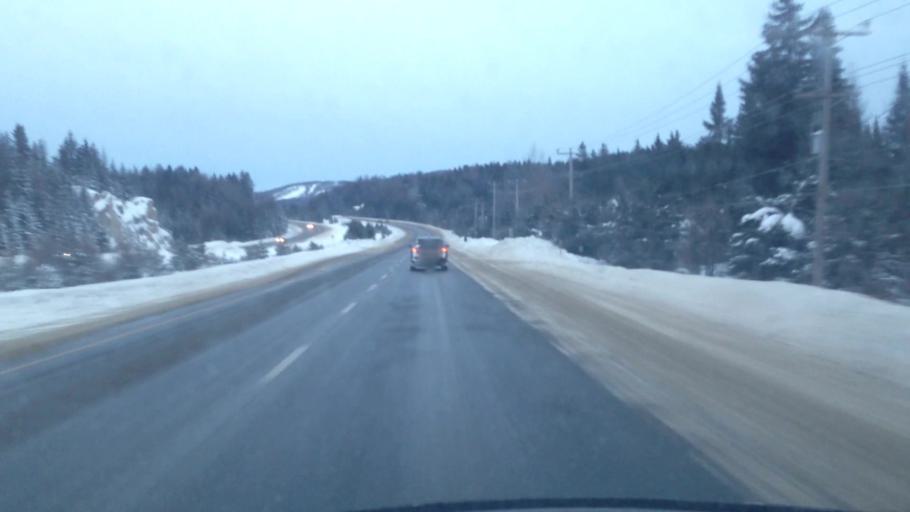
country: CA
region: Quebec
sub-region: Laurentides
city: Mont-Tremblant
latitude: 46.1141
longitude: -74.5447
